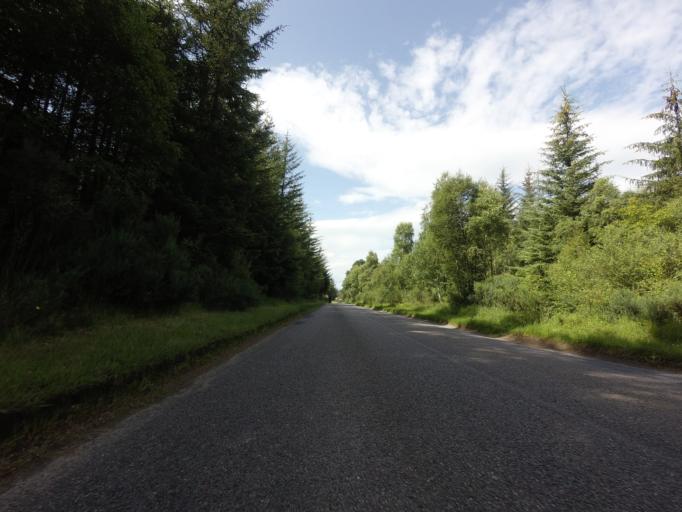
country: GB
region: Scotland
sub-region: Highland
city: Fortrose
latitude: 57.4835
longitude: -4.0930
